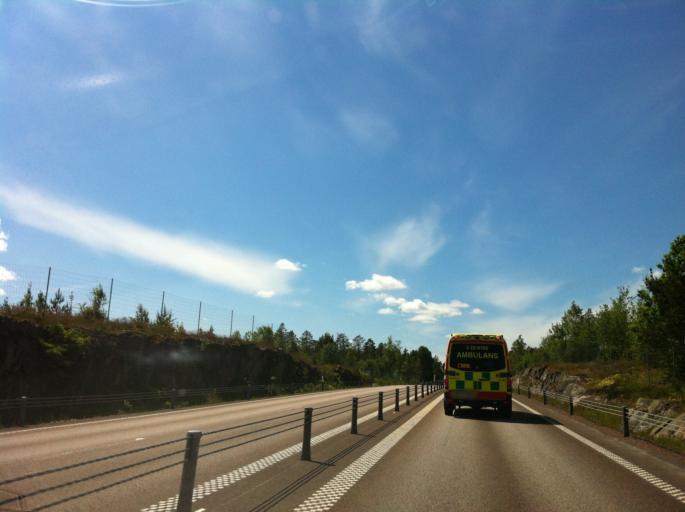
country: SE
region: Vaestra Goetaland
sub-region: Melleruds Kommun
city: Mellerud
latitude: 58.8470
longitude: 12.5510
